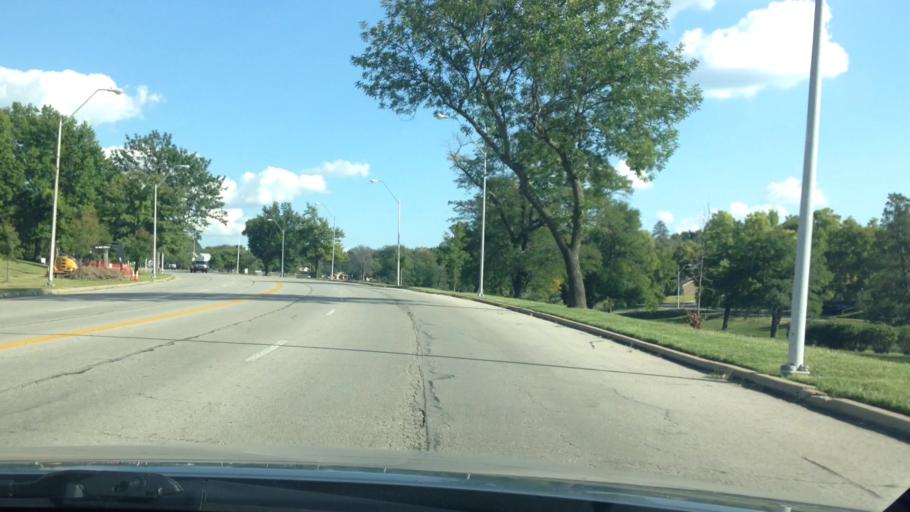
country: US
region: Kansas
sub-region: Johnson County
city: Mission Hills
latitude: 39.0089
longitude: -94.5669
